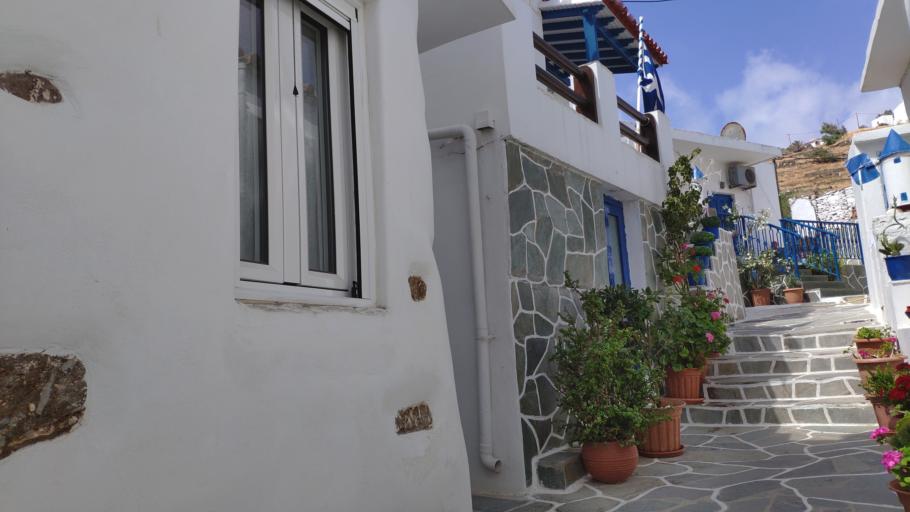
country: GR
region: South Aegean
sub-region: Nomos Kykladon
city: Kythnos
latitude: 37.3820
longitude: 24.4306
